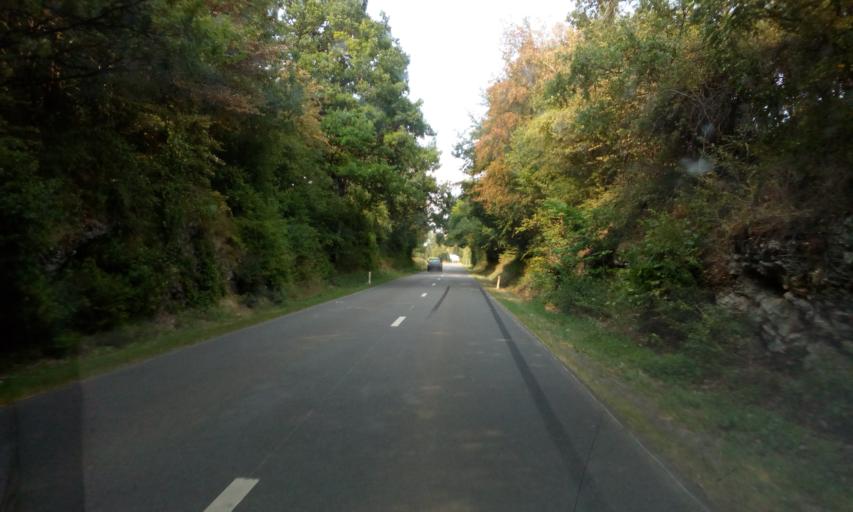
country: BE
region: Wallonia
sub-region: Province du Luxembourg
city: Tellin
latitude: 50.1102
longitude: 5.2390
